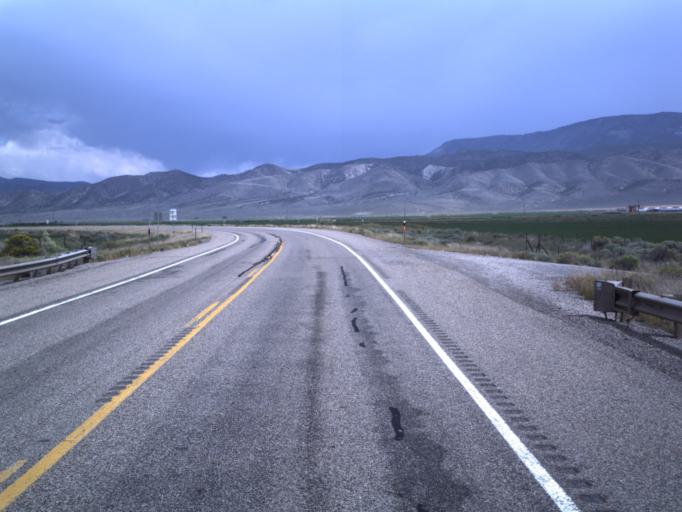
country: US
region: Utah
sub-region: Piute County
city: Junction
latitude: 38.1718
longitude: -112.2628
